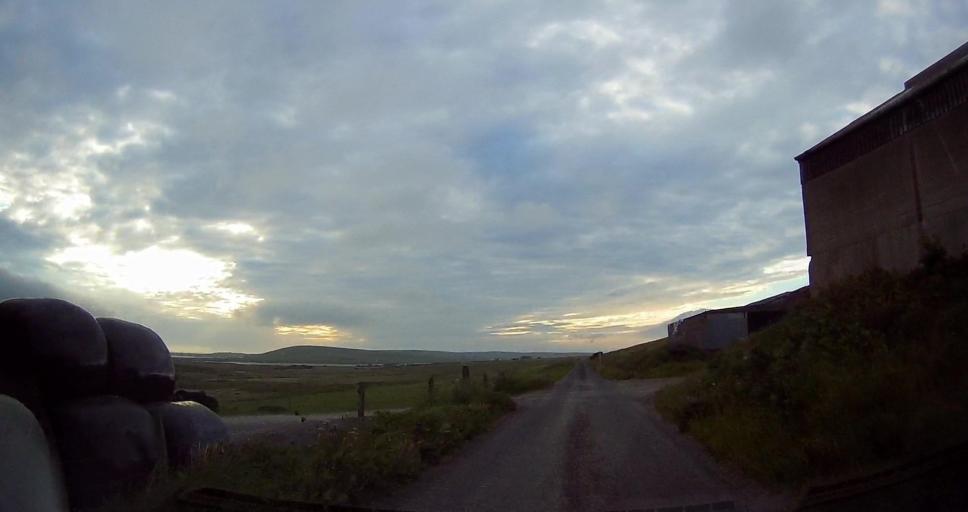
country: GB
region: Scotland
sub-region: Orkney Islands
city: Stromness
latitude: 59.1020
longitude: -3.2103
